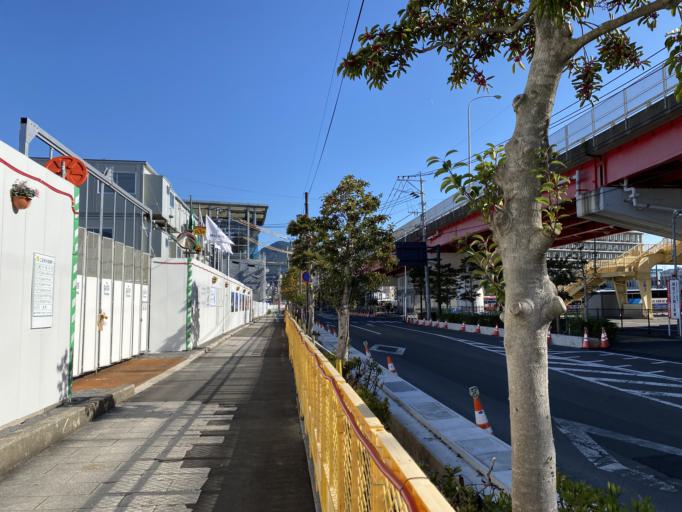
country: JP
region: Nagasaki
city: Nagasaki-shi
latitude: 32.7514
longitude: 129.8676
